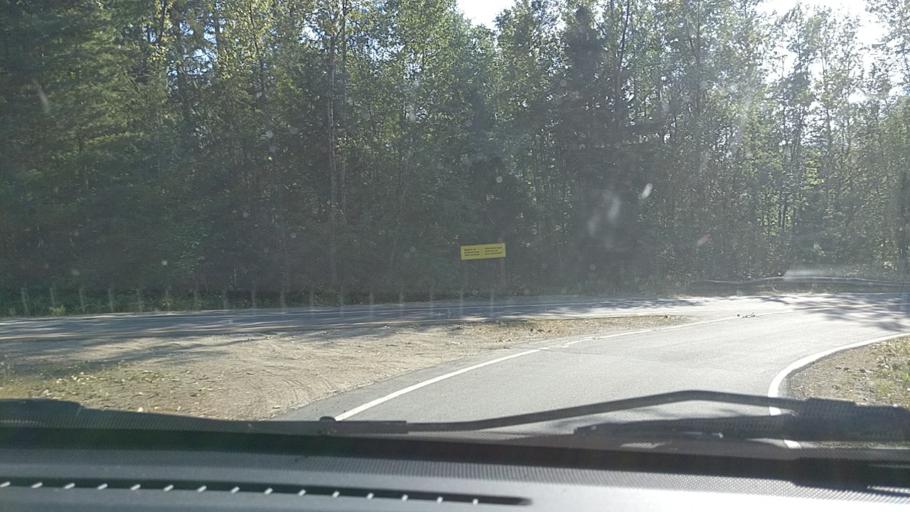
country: CA
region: British Columbia
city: Revelstoke
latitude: 51.0054
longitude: -118.1977
